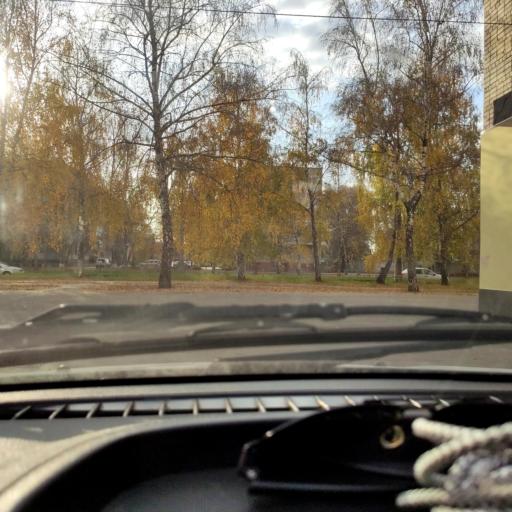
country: RU
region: Samara
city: Tol'yatti
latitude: 53.5316
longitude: 49.4168
